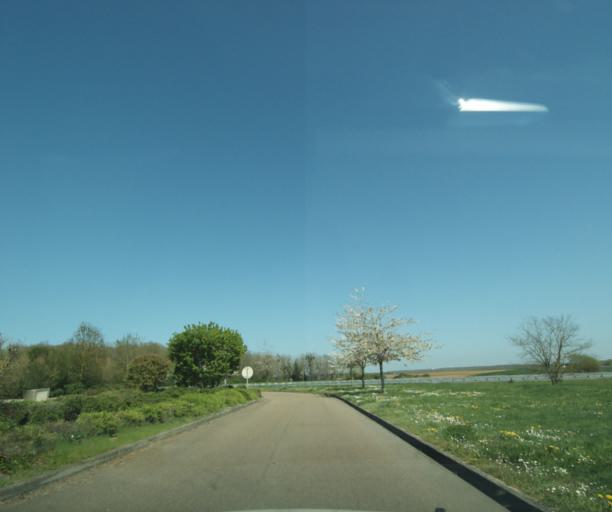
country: FR
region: Bourgogne
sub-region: Departement de la Nievre
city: Pouilly-sur-Loire
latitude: 47.3375
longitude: 2.9292
